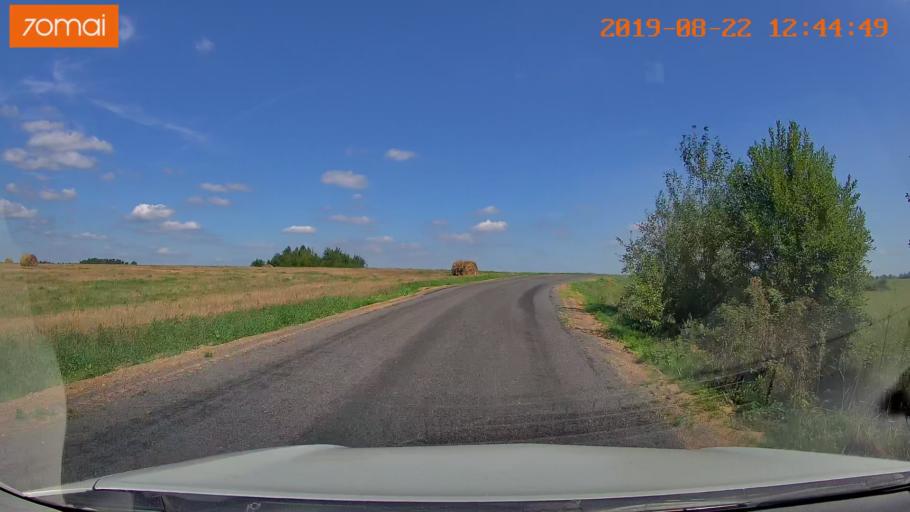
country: BY
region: Minsk
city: Prawdzinski
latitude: 53.4537
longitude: 27.6142
